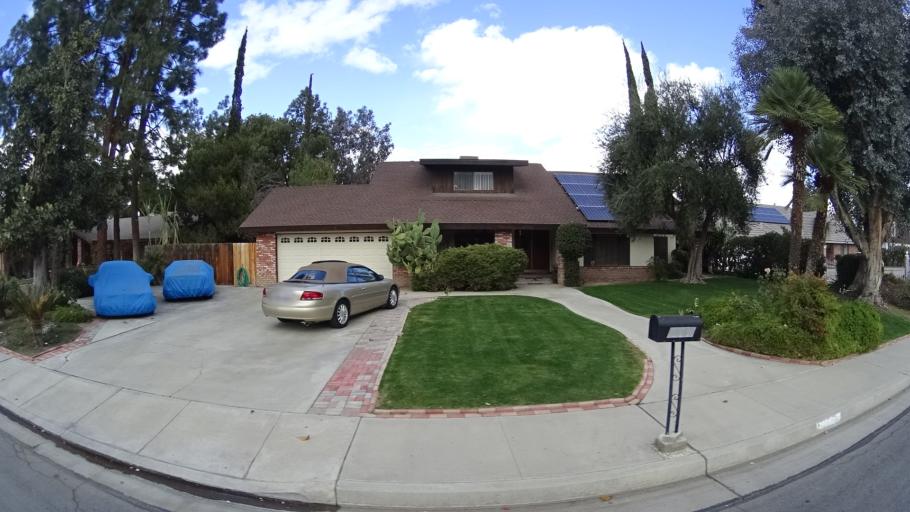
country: US
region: California
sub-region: Kern County
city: Greenacres
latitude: 35.3601
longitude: -119.0834
